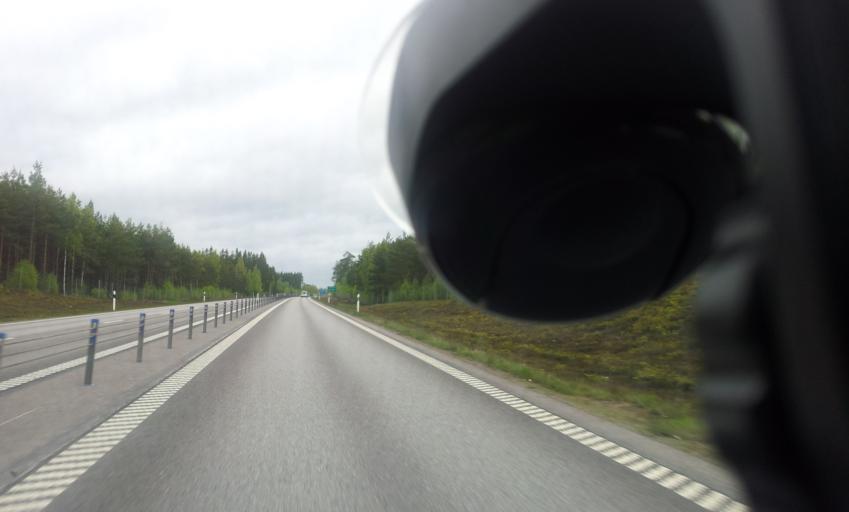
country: SE
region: Kalmar
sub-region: Kalmar Kommun
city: Ljungbyholm
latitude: 56.5384
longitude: 16.0839
